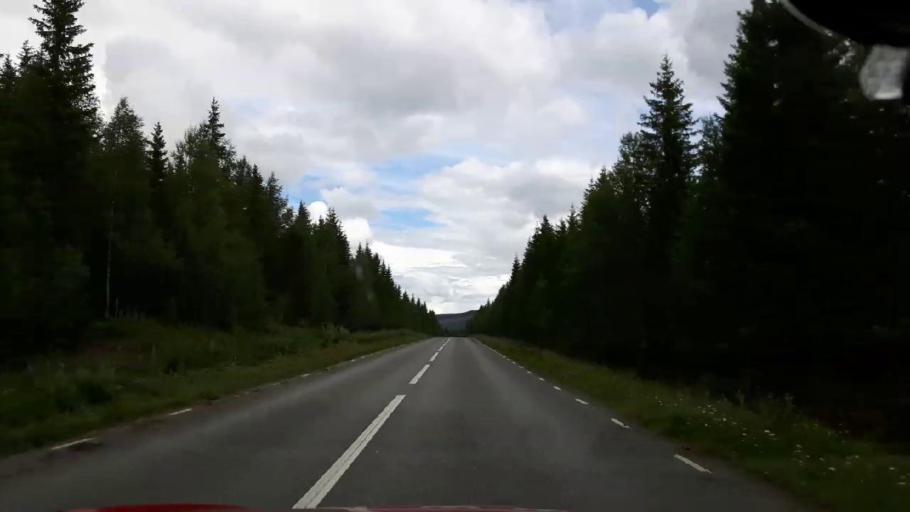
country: NO
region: Nord-Trondelag
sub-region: Lierne
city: Sandvika
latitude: 64.3902
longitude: 14.4591
